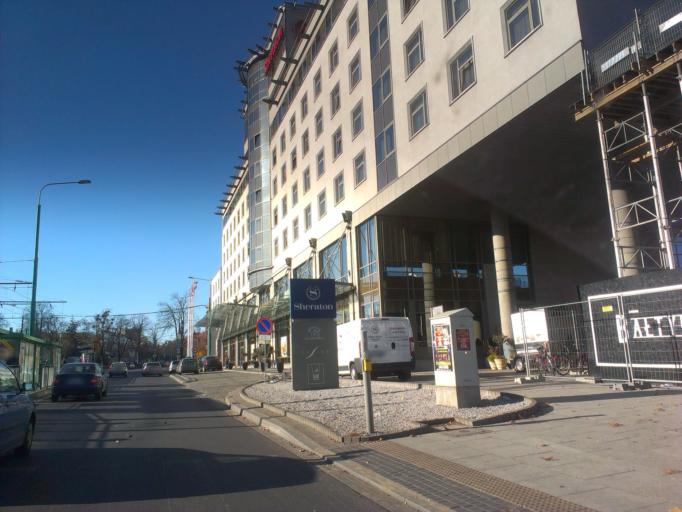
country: PL
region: Greater Poland Voivodeship
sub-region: Poznan
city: Poznan
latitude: 52.4066
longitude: 16.9117
